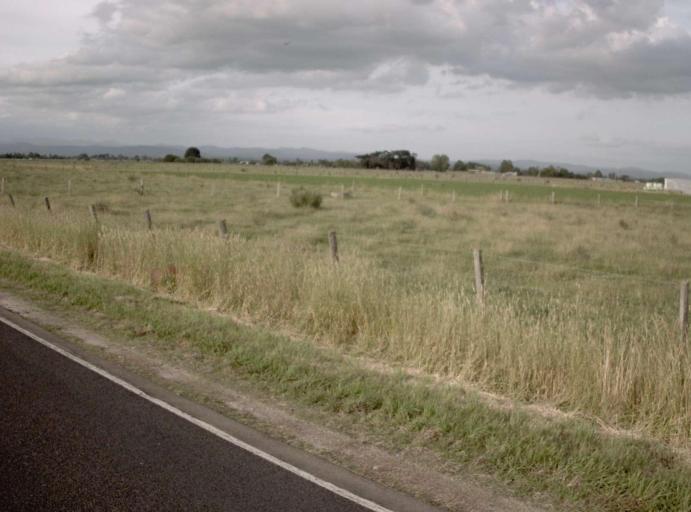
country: AU
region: Victoria
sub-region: Wellington
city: Heyfield
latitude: -37.8946
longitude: 146.9914
